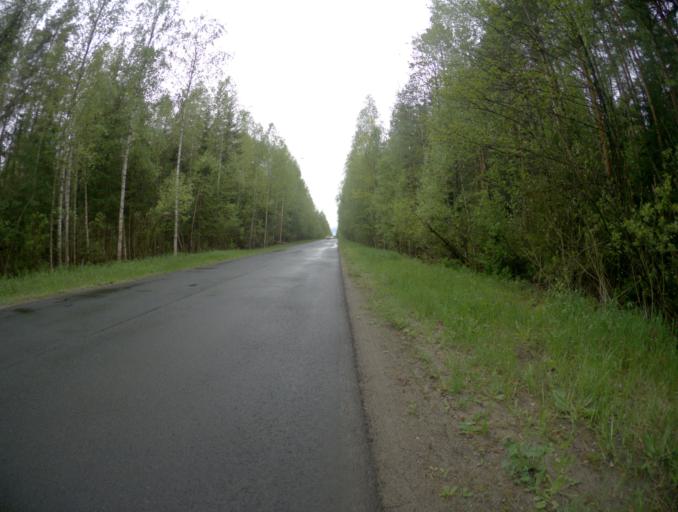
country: RU
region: Vladimir
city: Zolotkovo
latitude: 55.3456
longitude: 40.9825
